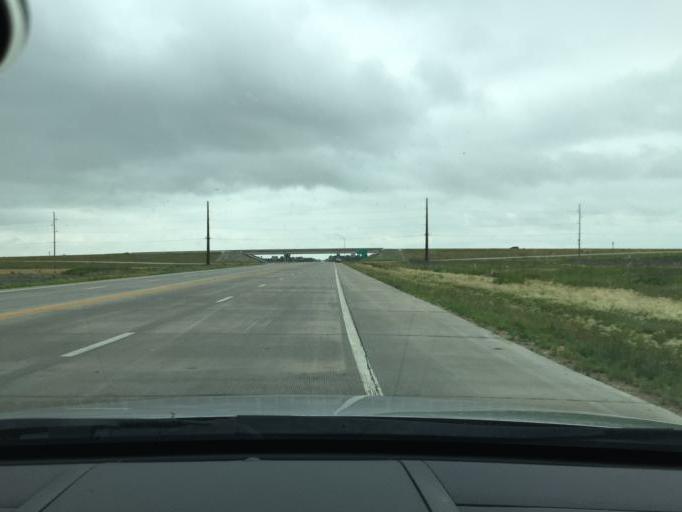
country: US
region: Kansas
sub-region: Reno County
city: Hutchinson
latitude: 38.0320
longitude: -97.8669
